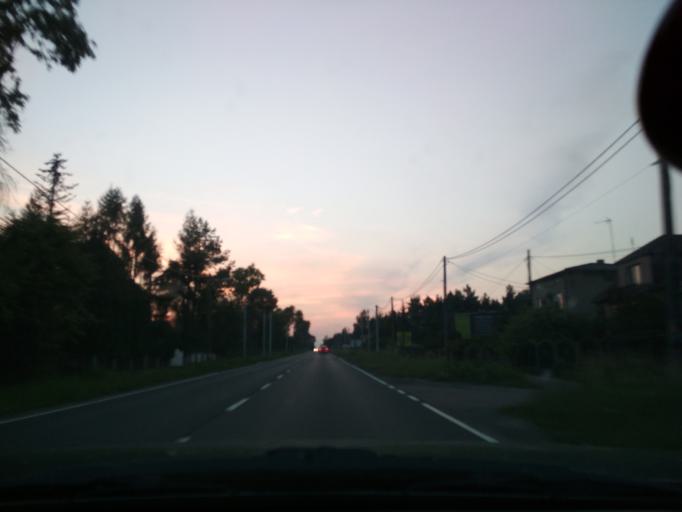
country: PL
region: Silesian Voivodeship
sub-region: Powiat zawiercianski
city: Ogrodzieniec
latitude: 50.4714
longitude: 19.4817
